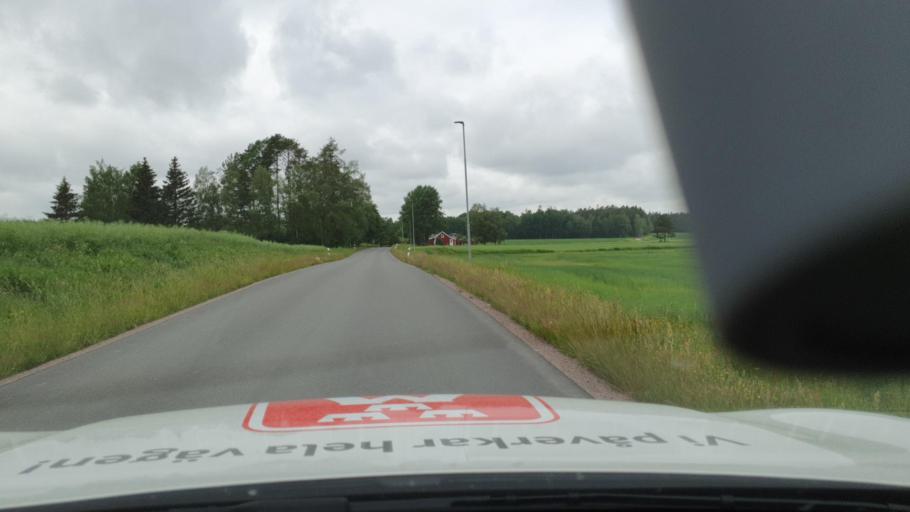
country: SE
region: Vaestra Goetaland
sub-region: Tibro Kommun
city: Tibro
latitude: 58.4071
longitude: 14.1752
